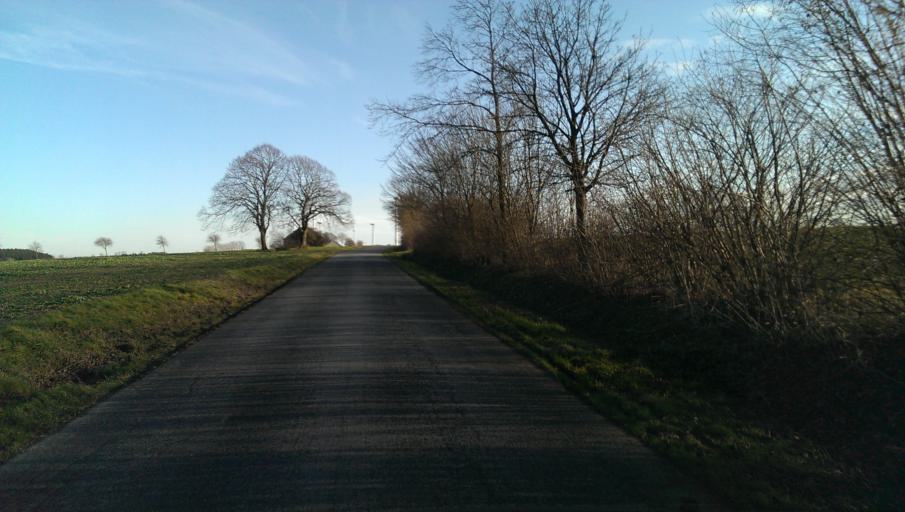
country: DE
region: North Rhine-Westphalia
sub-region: Regierungsbezirk Arnsberg
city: Ruthen
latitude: 51.5209
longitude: 8.4224
